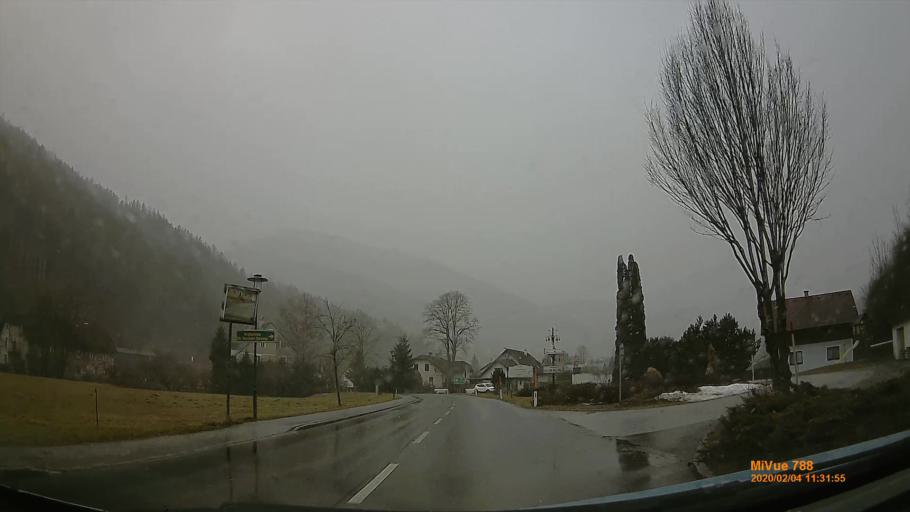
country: AT
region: Styria
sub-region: Politischer Bezirk Bruck-Muerzzuschlag
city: Neuberg an der Muerz
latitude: 47.6597
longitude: 15.5862
